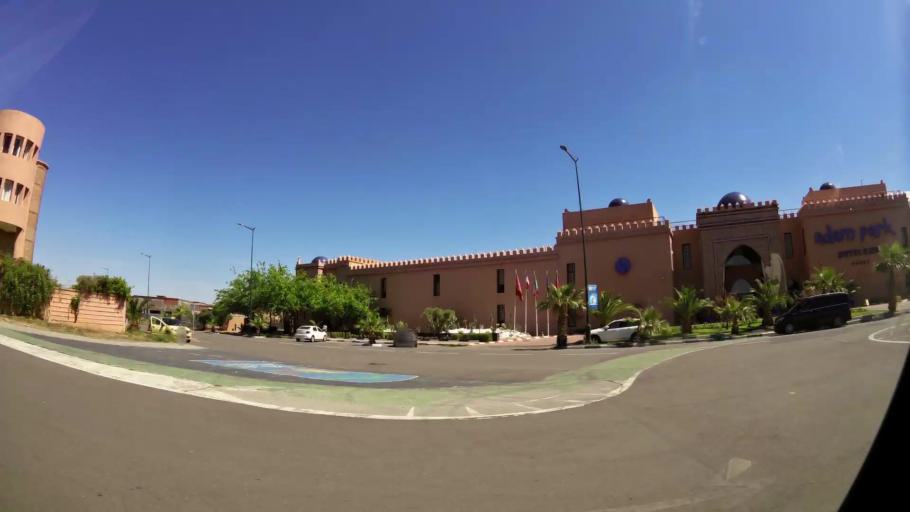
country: MA
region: Marrakech-Tensift-Al Haouz
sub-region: Marrakech
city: Marrakesh
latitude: 31.5963
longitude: -7.9903
